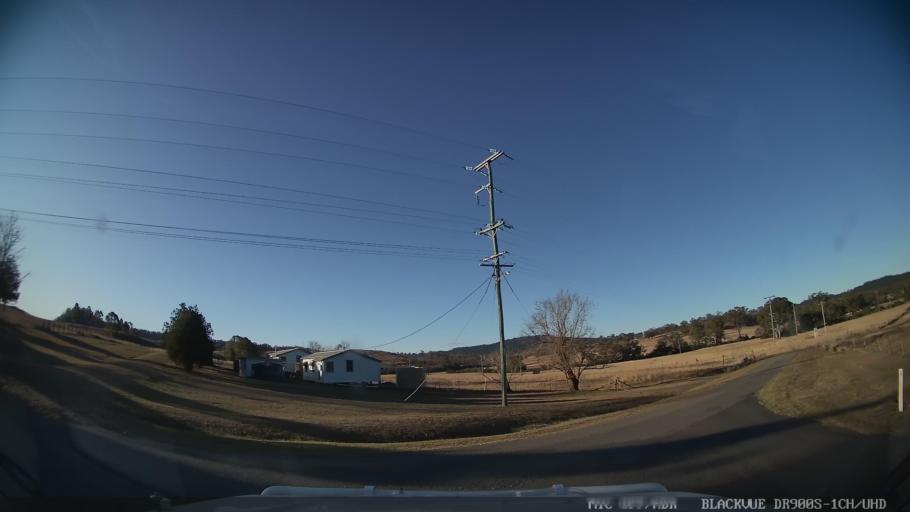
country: AU
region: Queensland
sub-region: Gladstone
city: Toolooa
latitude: -24.6932
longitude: 151.3057
